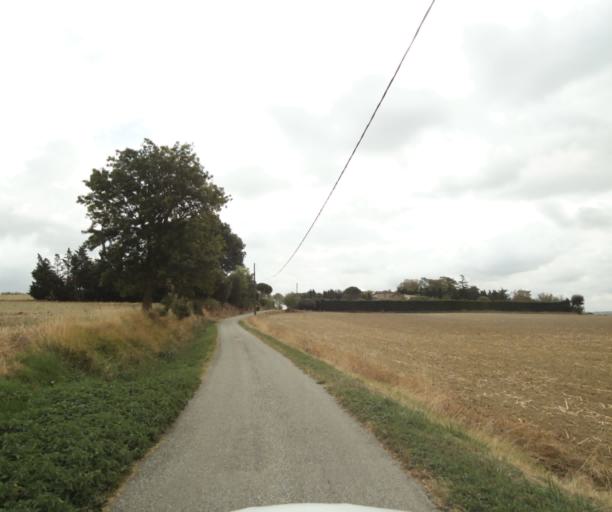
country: FR
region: Midi-Pyrenees
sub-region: Departement de la Haute-Garonne
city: Villefranche-de-Lauragais
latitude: 43.4155
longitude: 1.7125
